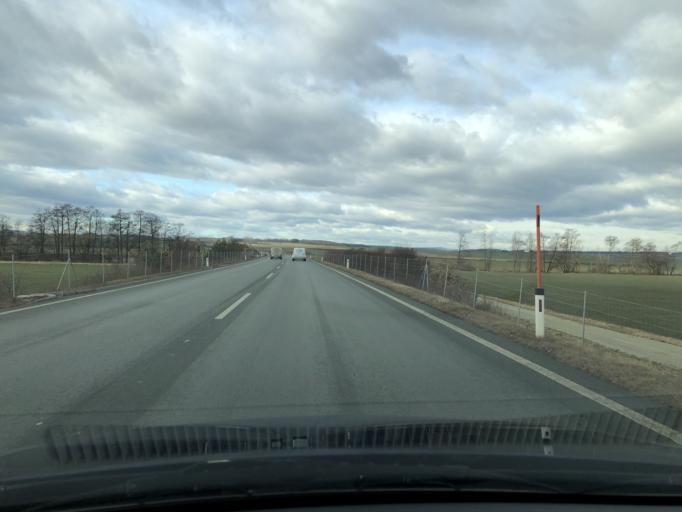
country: AT
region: Burgenland
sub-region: Politischer Bezirk Oberwart
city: Markt Neuhodis
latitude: 47.2761
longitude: 16.4060
